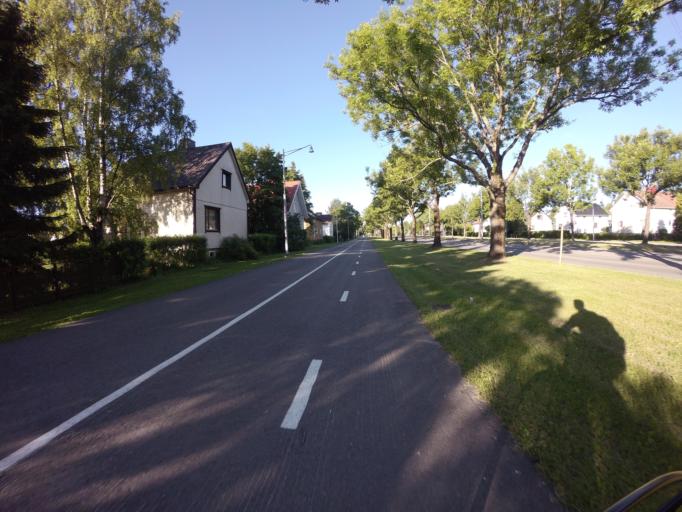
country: FI
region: Varsinais-Suomi
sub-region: Turku
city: Turku
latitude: 60.4706
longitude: 22.2815
